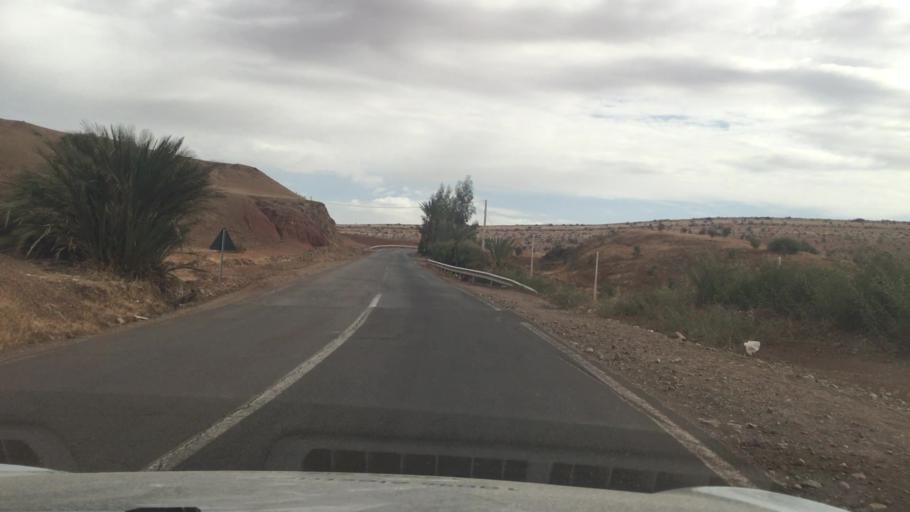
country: MA
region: Marrakech-Tensift-Al Haouz
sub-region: Al-Haouz
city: Touama
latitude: 31.5460
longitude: -7.5662
